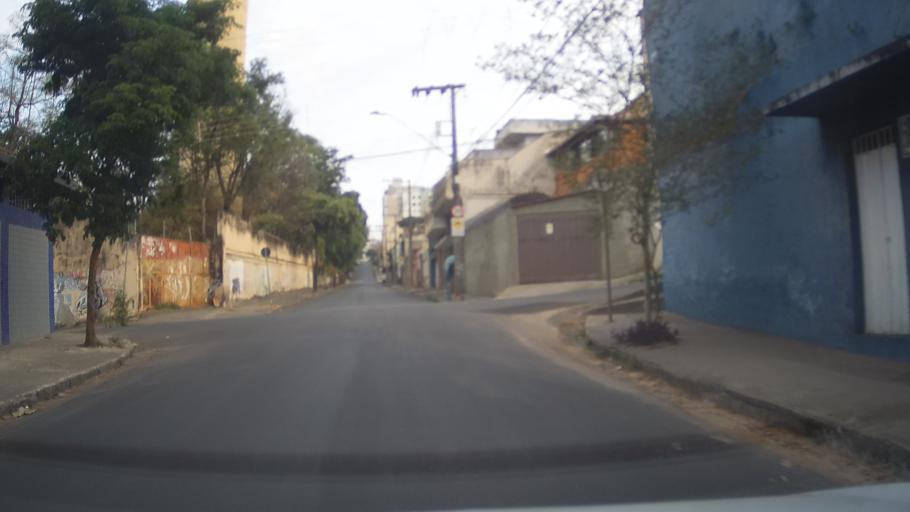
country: BR
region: Minas Gerais
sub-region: Belo Horizonte
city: Belo Horizonte
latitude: -19.8929
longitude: -43.9333
